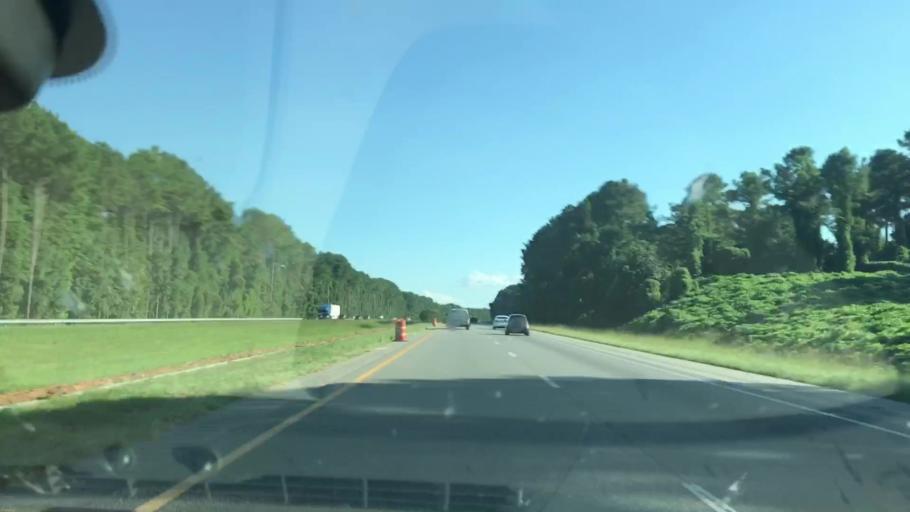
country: US
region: Georgia
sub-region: Harris County
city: Hamilton
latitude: 32.7911
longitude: -85.0210
